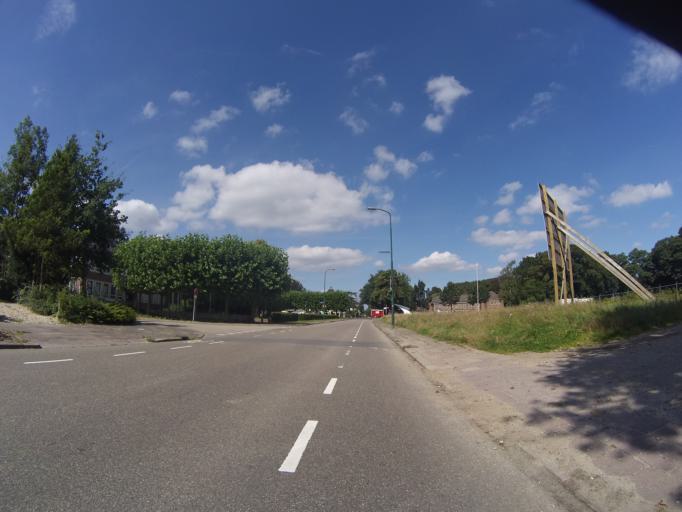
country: NL
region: Utrecht
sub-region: Gemeente Soest
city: Soest
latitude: 52.1202
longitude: 5.2860
